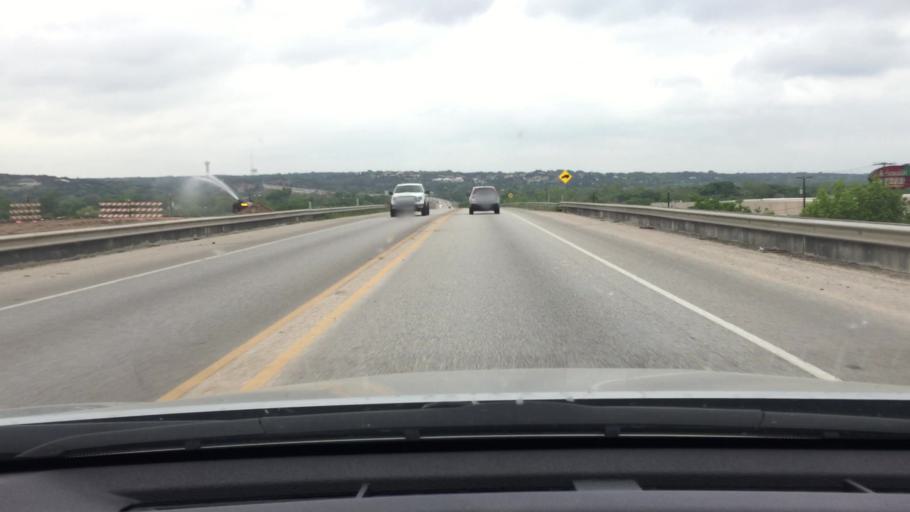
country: US
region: Texas
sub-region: Comal County
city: New Braunfels
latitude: 29.6823
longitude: -98.1549
